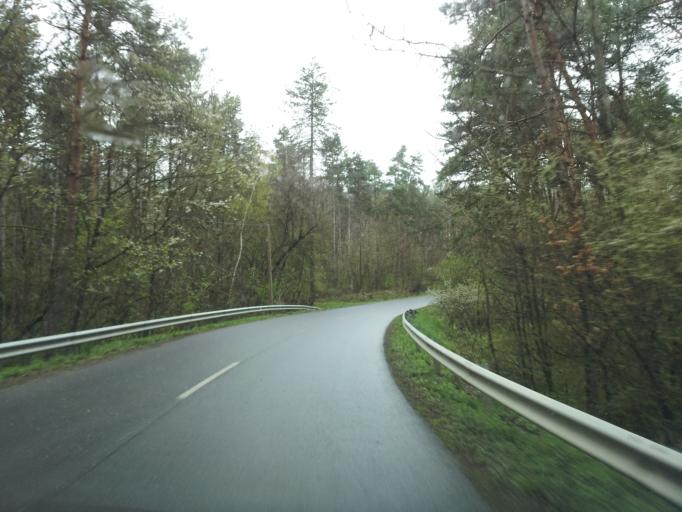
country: HU
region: Borsod-Abauj-Zemplen
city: Putnok
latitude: 48.4531
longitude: 20.4788
